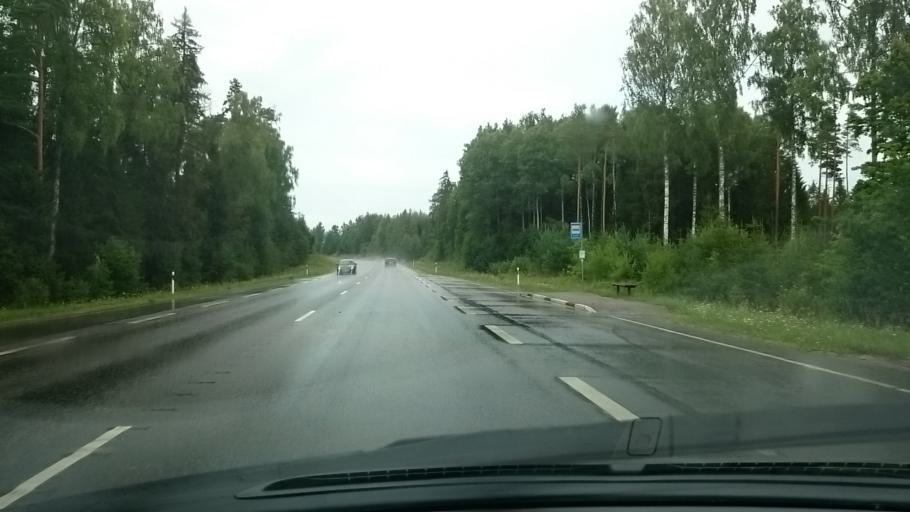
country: EE
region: Tartu
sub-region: UElenurme vald
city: Ulenurme
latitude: 58.1228
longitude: 26.7314
